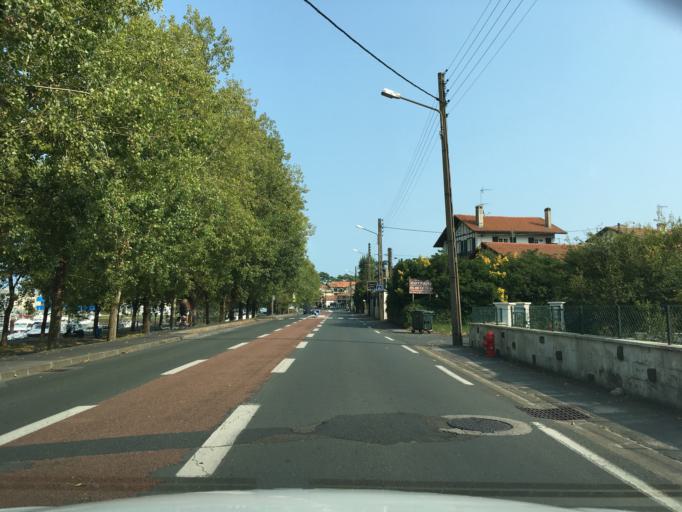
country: FR
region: Aquitaine
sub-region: Departement des Pyrenees-Atlantiques
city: Boucau
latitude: 43.5256
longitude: -1.5101
